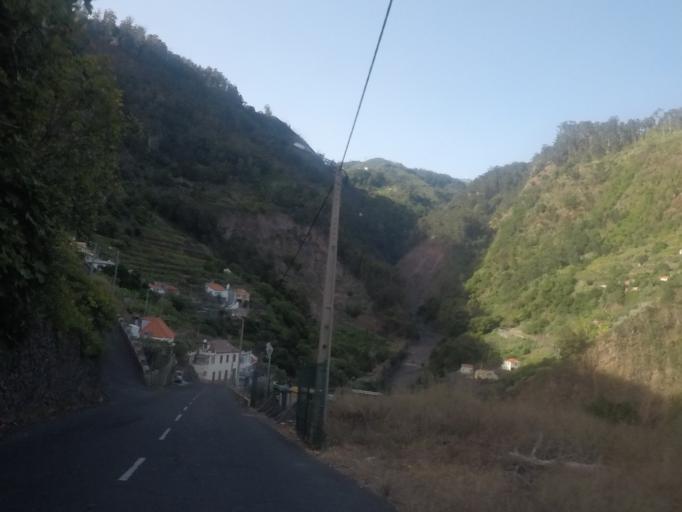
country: PT
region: Madeira
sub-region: Calheta
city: Arco da Calheta
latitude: 32.7113
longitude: -17.1351
